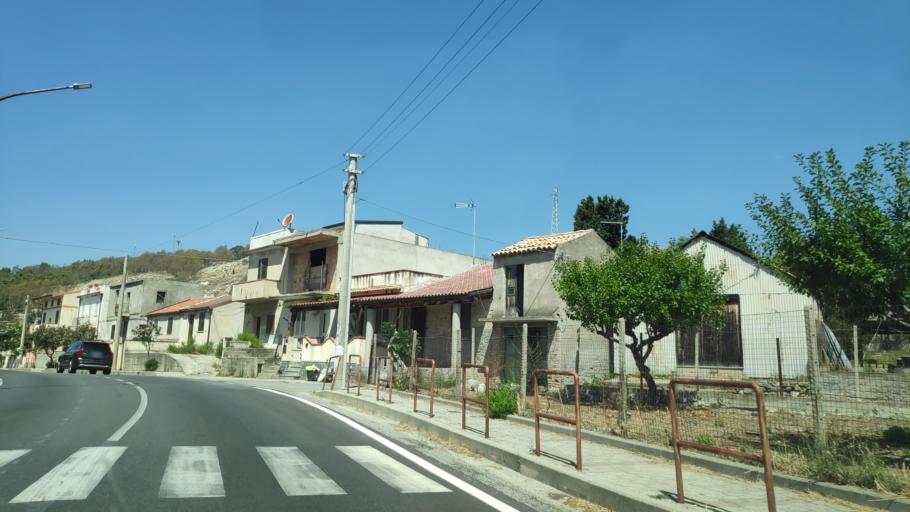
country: IT
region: Calabria
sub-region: Provincia di Reggio Calabria
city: Palizzi Marina
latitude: 37.9243
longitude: 16.0403
